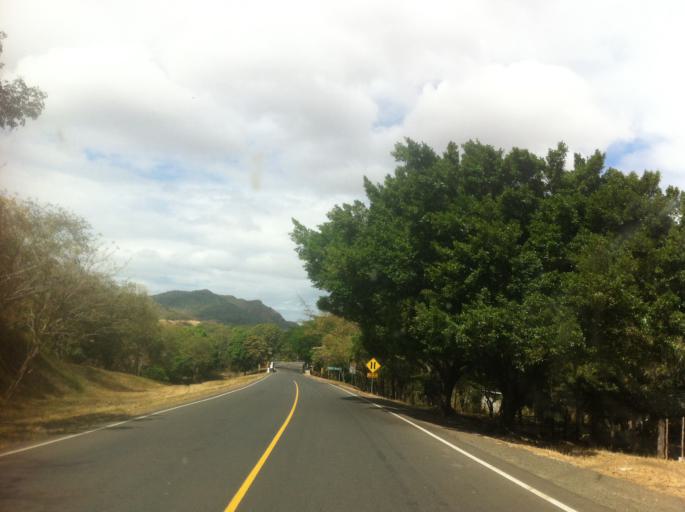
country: NI
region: Chontales
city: Juigalpa
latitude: 12.0486
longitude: -85.2901
